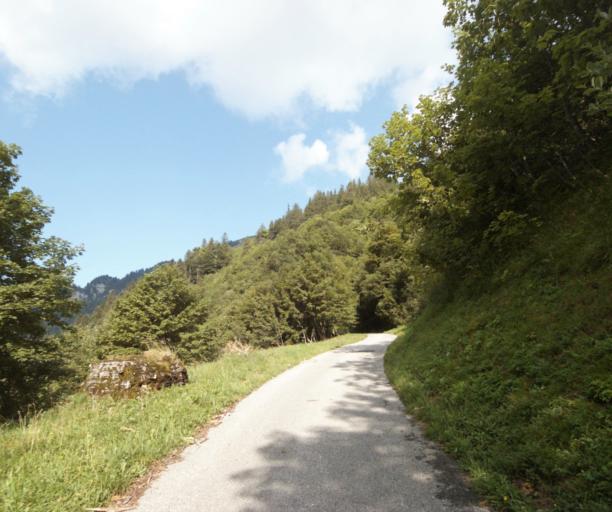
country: CH
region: Vaud
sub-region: Riviera-Pays-d'Enhaut District
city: Caux
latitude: 46.4219
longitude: 6.9850
